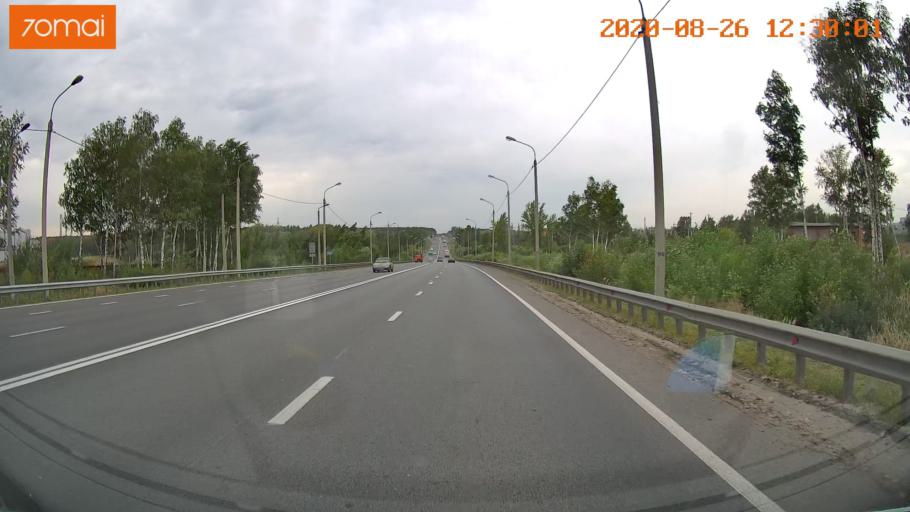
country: RU
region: Rjazan
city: Ryazan'
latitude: 54.5677
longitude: 39.8097
